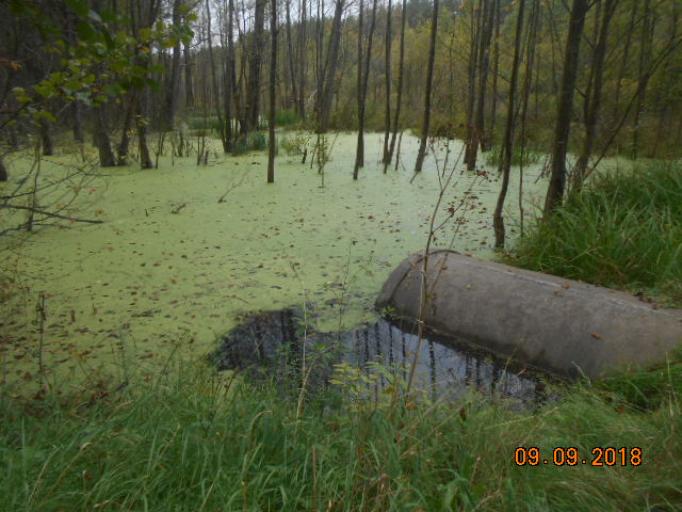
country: BY
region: Brest
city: Baranovichi
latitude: 53.1138
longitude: 25.6923
